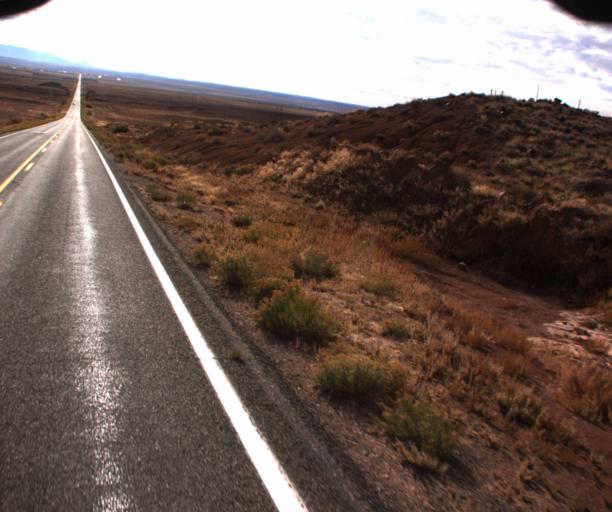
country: US
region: Arizona
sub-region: Apache County
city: Many Farms
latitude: 36.5439
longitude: -109.5282
